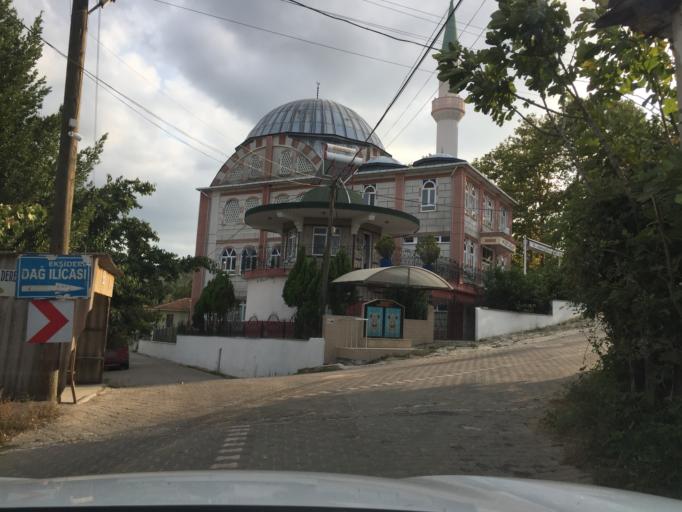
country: TR
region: Balikesir
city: Gonen
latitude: 40.0485
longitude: 27.5834
